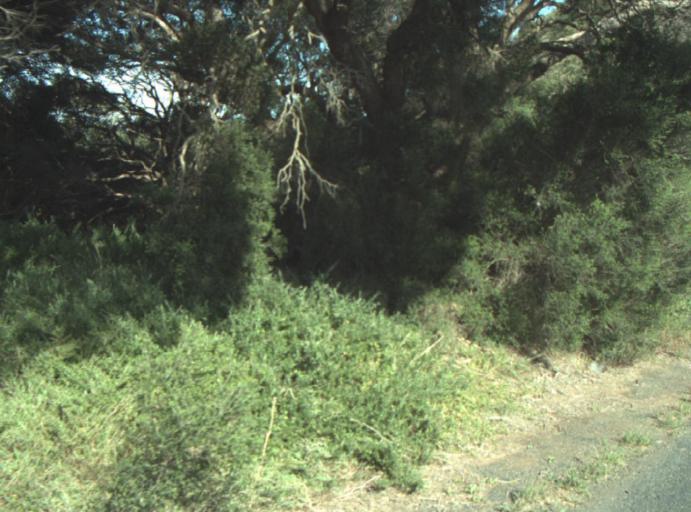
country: AU
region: Victoria
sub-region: Greater Geelong
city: Leopold
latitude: -38.2563
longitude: 144.5046
